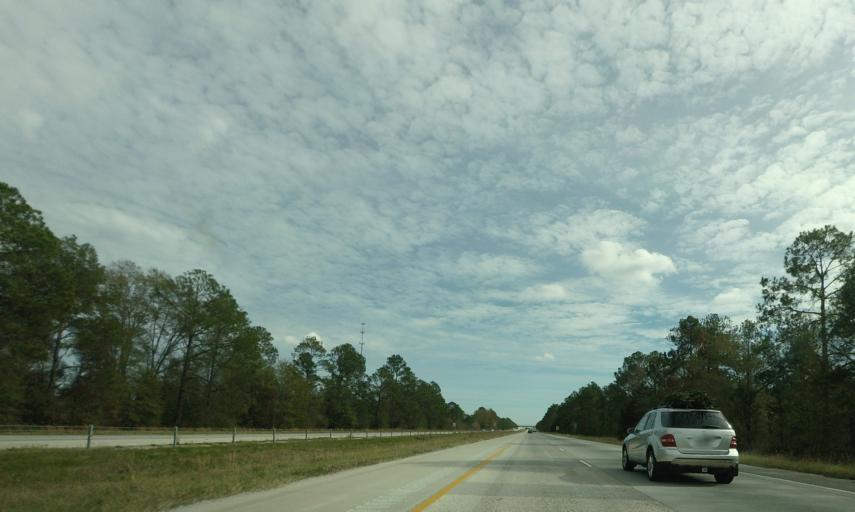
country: US
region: Georgia
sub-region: Laurens County
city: Dublin
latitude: 32.5078
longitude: -83.0403
